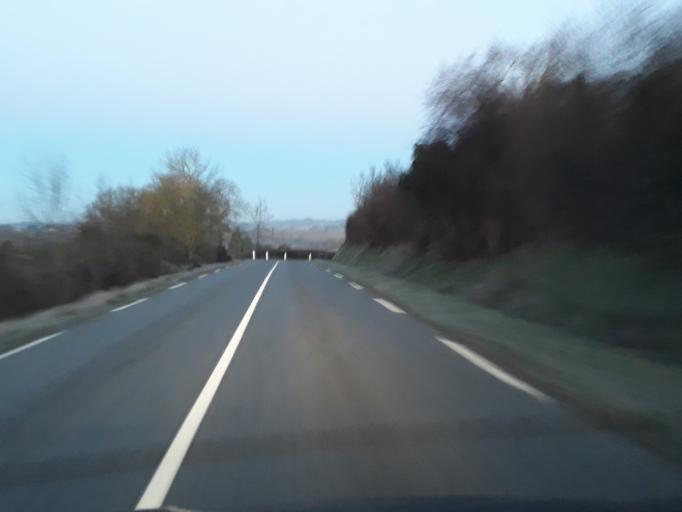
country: FR
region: Midi-Pyrenees
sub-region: Departement du Gers
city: Samatan
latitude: 43.4711
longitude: 0.9656
